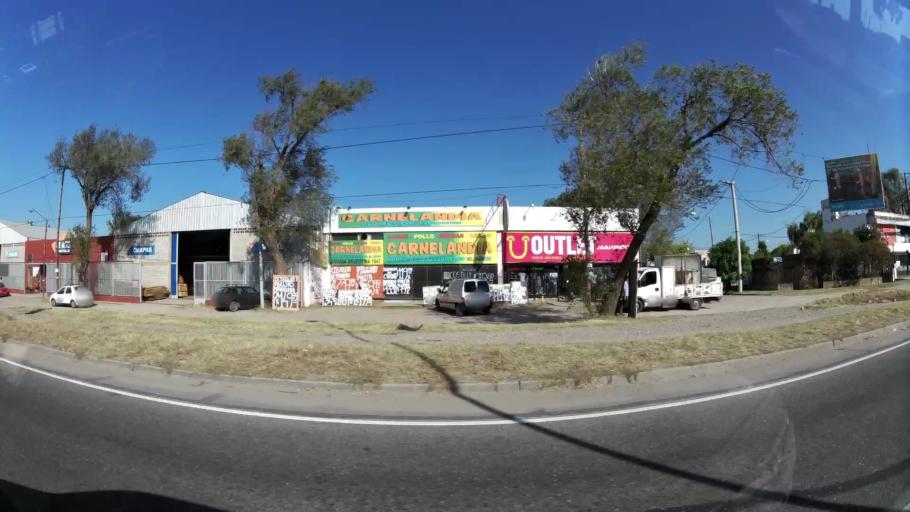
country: AR
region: Cordoba
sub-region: Departamento de Capital
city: Cordoba
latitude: -31.4708
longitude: -64.2289
